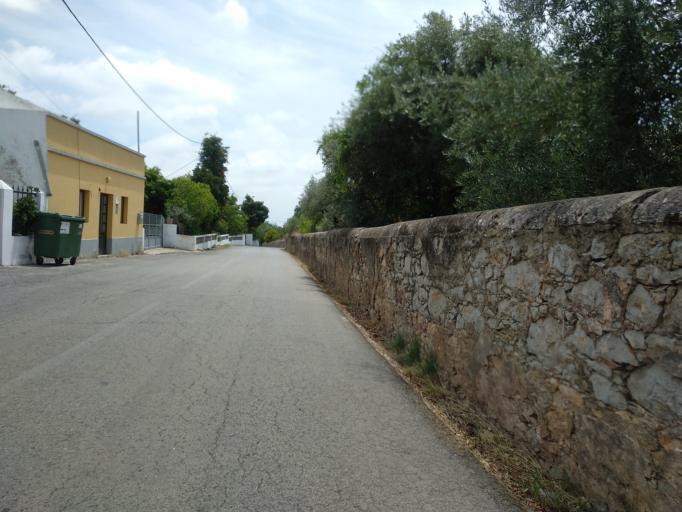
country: PT
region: Faro
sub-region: Sao Bras de Alportel
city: Sao Bras de Alportel
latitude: 37.1610
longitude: -7.8850
